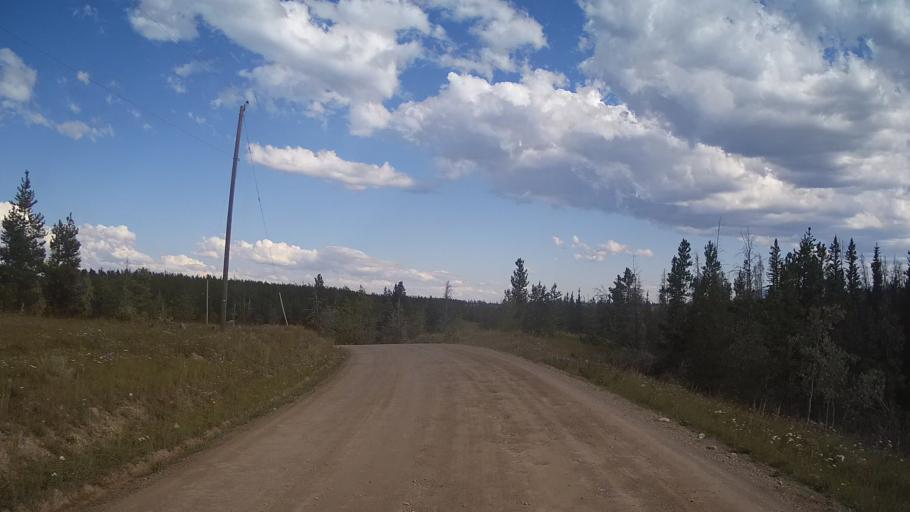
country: CA
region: British Columbia
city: Lillooet
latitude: 51.2878
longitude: -121.7508
